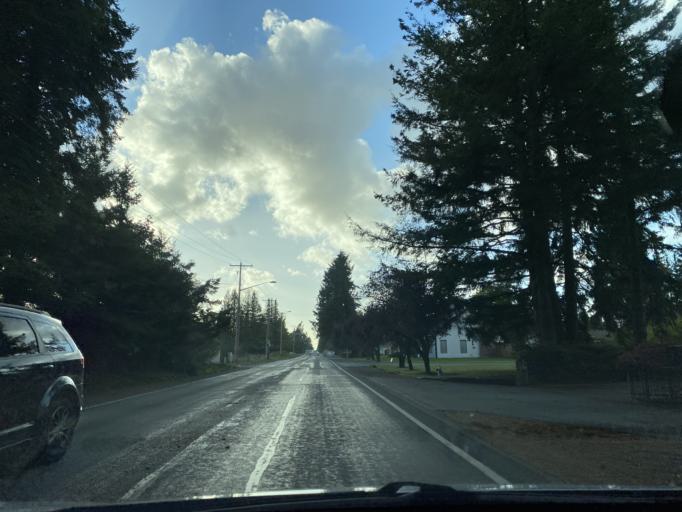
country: US
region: Washington
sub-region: Pierce County
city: South Hill
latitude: 47.1184
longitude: -122.2764
